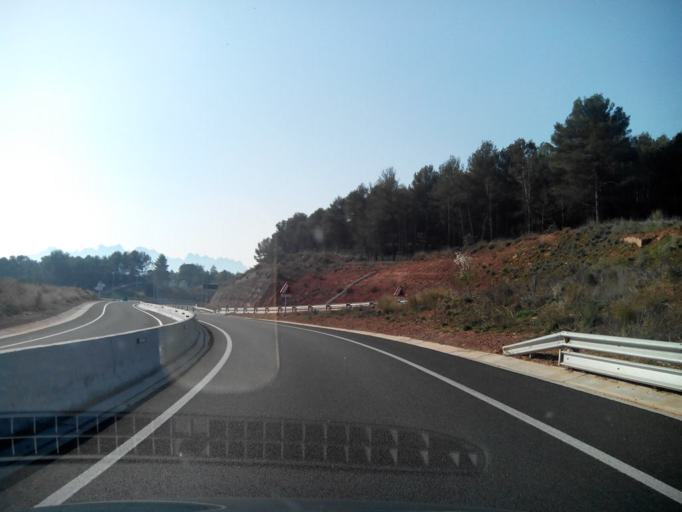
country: ES
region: Catalonia
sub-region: Provincia de Barcelona
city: Sant Joan de Vilatorrada
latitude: 41.7334
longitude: 1.7821
